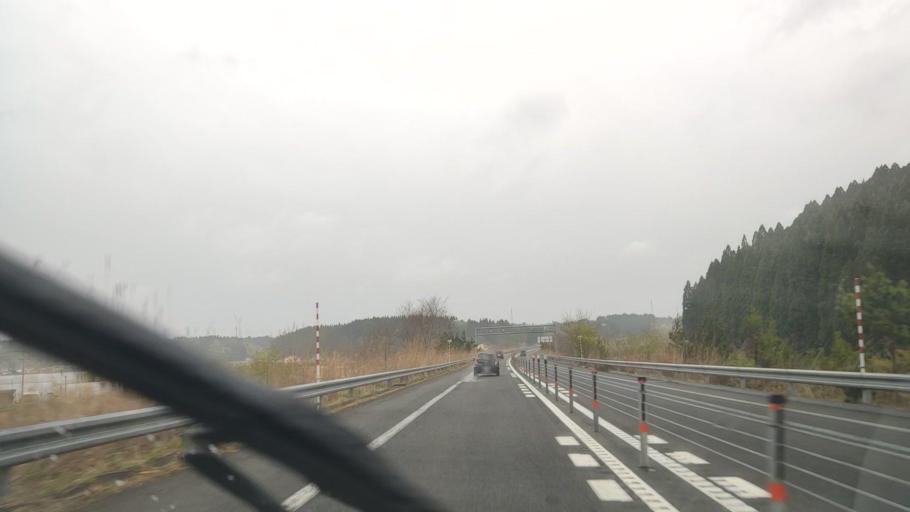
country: JP
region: Akita
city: Noshiromachi
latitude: 40.1884
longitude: 140.1014
